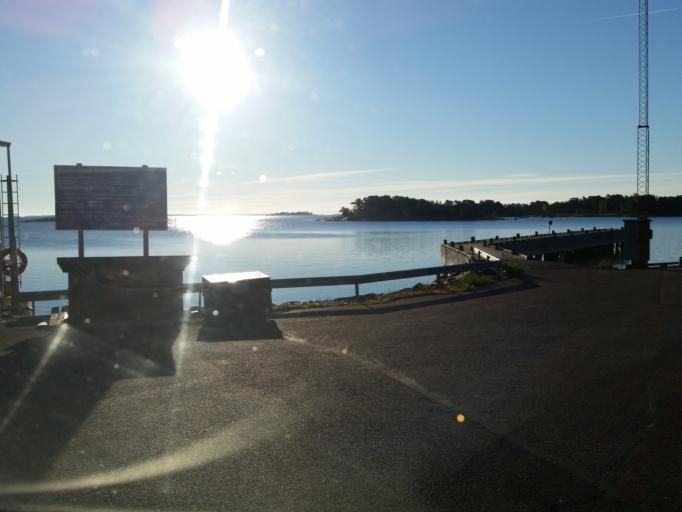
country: AX
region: Alands skaergard
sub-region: Vardoe
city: Vardoe
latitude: 60.2243
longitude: 20.4132
